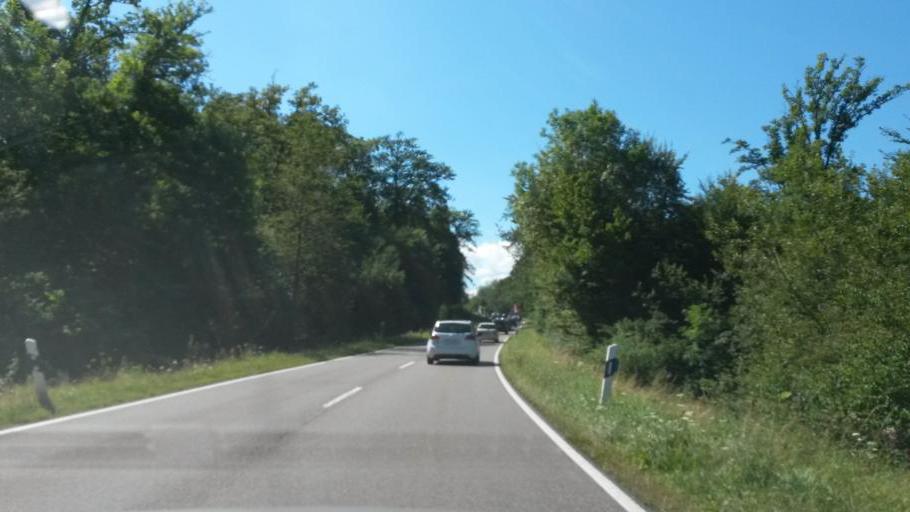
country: DE
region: Baden-Wuerttemberg
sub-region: Karlsruhe Region
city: Ispringen
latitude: 48.9070
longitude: 8.6277
